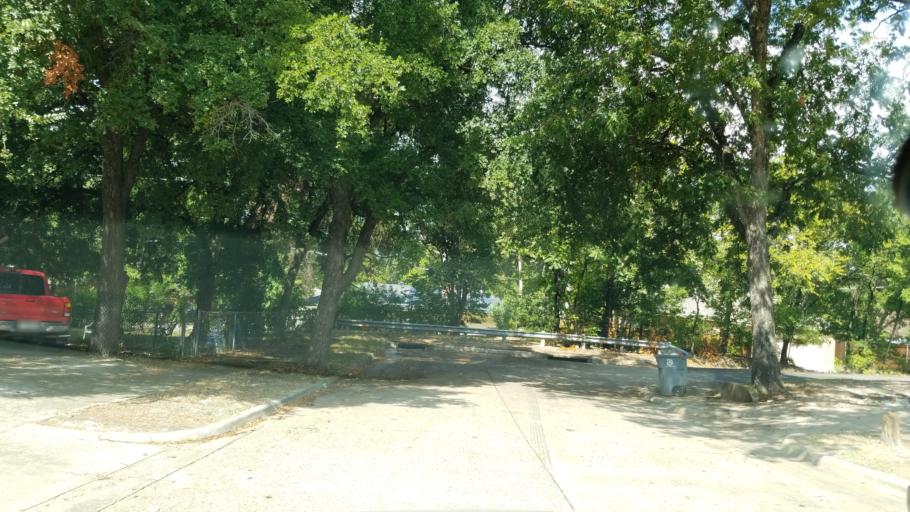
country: US
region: Texas
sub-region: Dallas County
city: Duncanville
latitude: 32.6692
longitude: -96.8351
